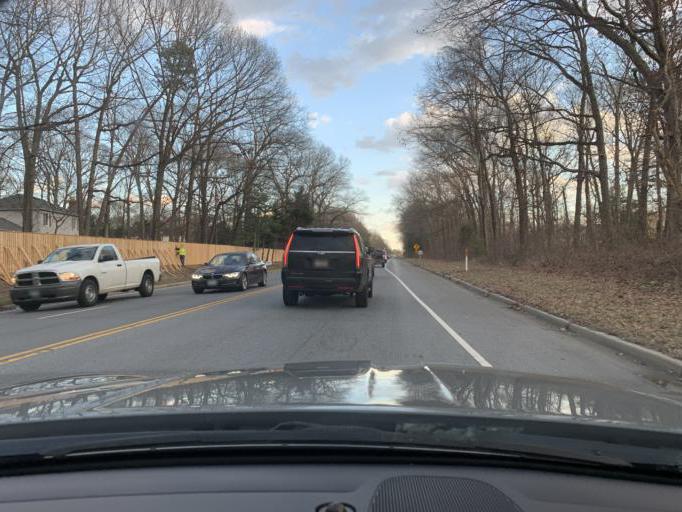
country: US
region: Maryland
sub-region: Anne Arundel County
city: South Gate
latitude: 39.0937
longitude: -76.6179
